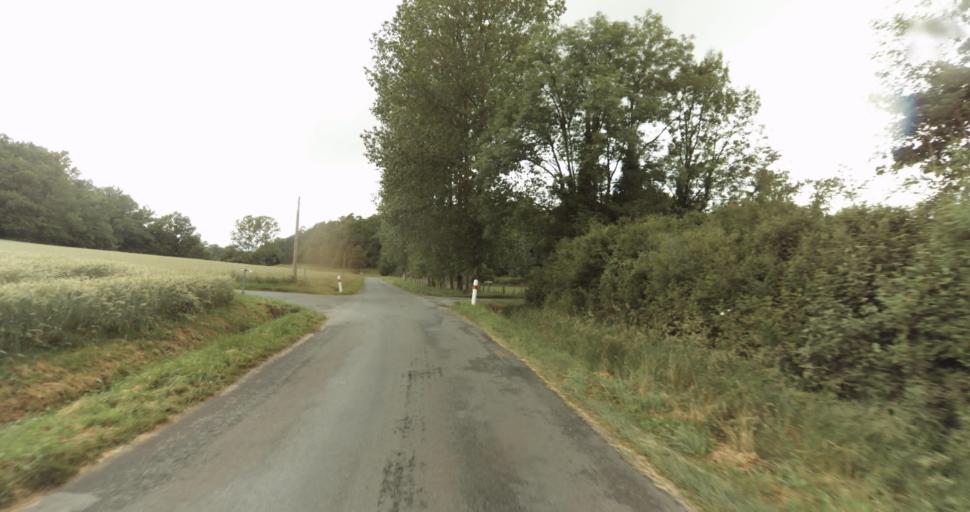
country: FR
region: Aquitaine
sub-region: Departement de la Dordogne
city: Belves
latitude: 44.7547
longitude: 0.9383
